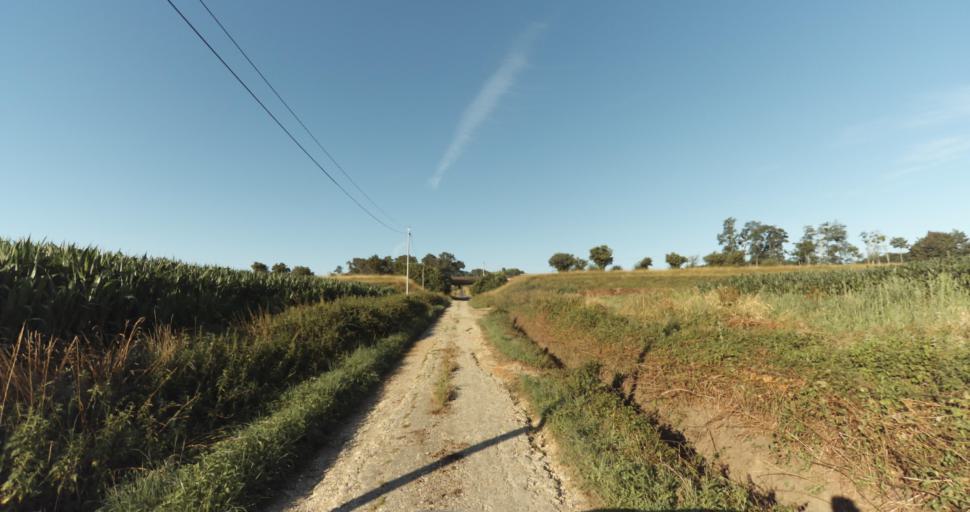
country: FR
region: Aquitaine
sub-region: Departement de la Gironde
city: Bazas
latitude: 44.4232
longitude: -0.2239
